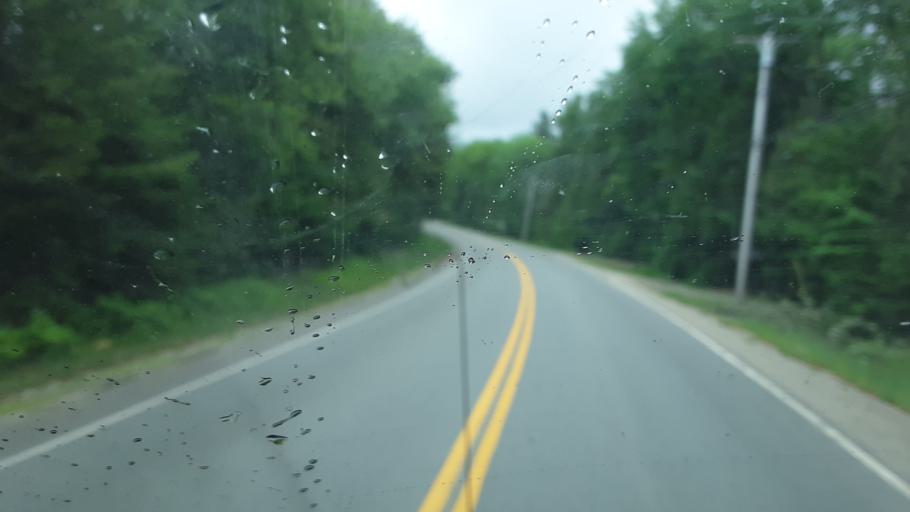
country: US
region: Maine
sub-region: Penobscot County
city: Millinocket
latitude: 45.6851
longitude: -68.7739
